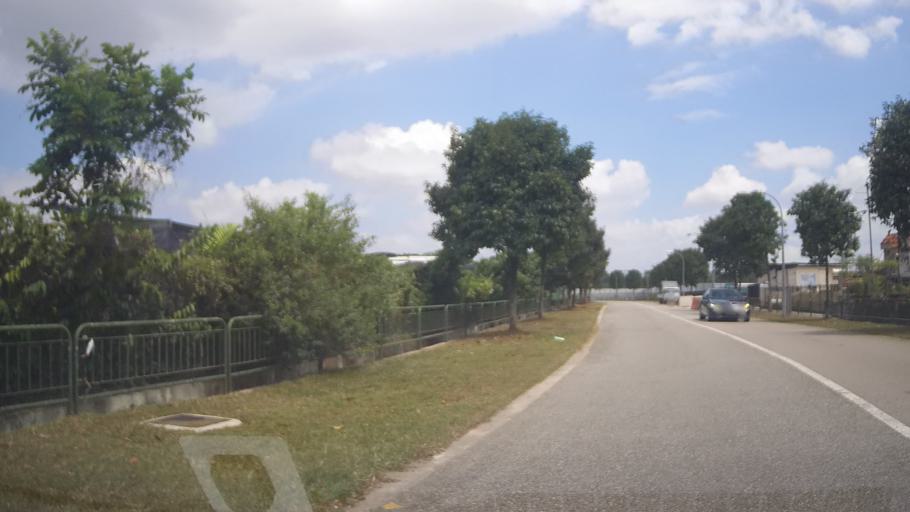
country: MY
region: Johor
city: Johor Bahru
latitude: 1.4409
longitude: 103.7282
